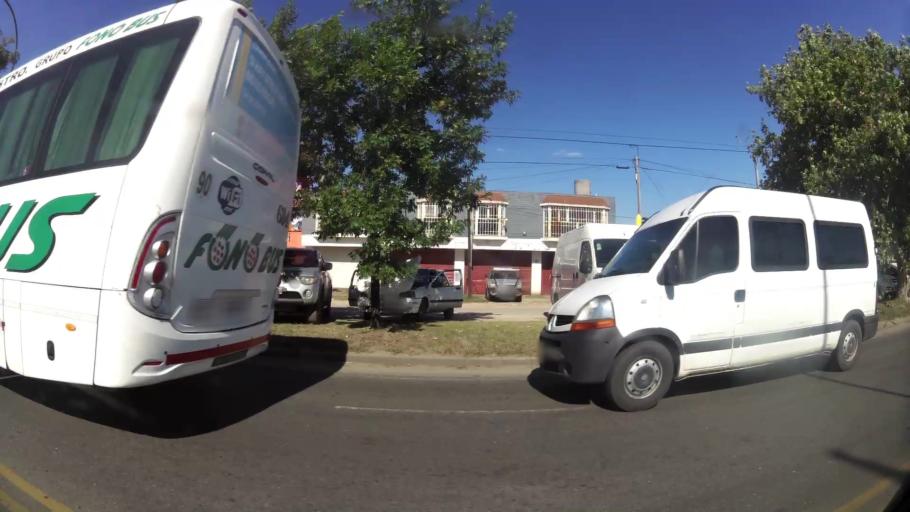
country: AR
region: Cordoba
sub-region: Departamento de Capital
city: Cordoba
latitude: -31.3669
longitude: -64.1761
